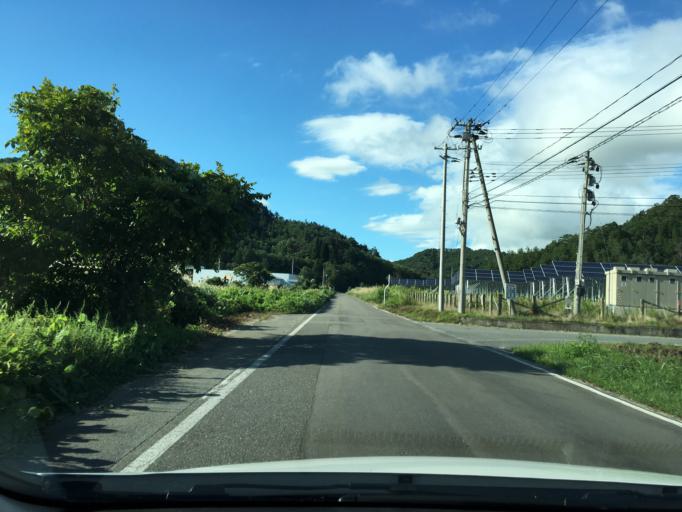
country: JP
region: Yamagata
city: Yonezawa
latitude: 37.8853
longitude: 140.1929
